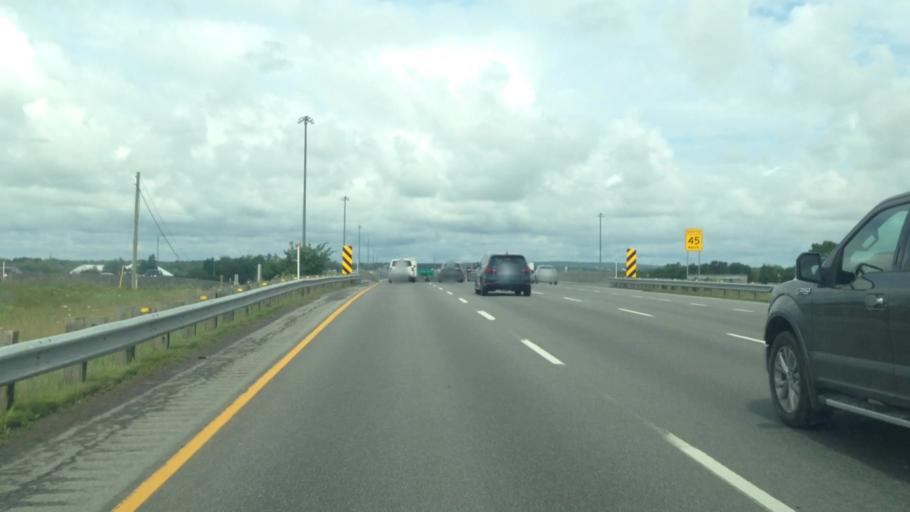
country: CA
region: Quebec
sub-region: Laurentides
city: Saint-Jerome
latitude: 45.7445
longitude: -74.0016
